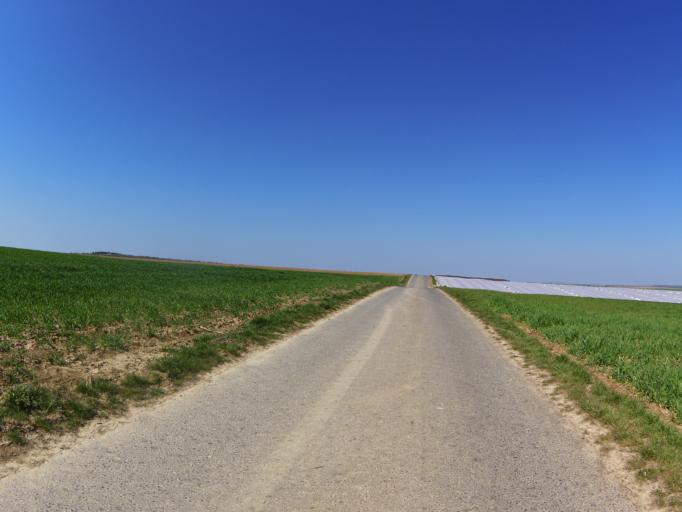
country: DE
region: Bavaria
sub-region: Regierungsbezirk Unterfranken
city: Biebelried
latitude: 49.8186
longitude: 10.0829
